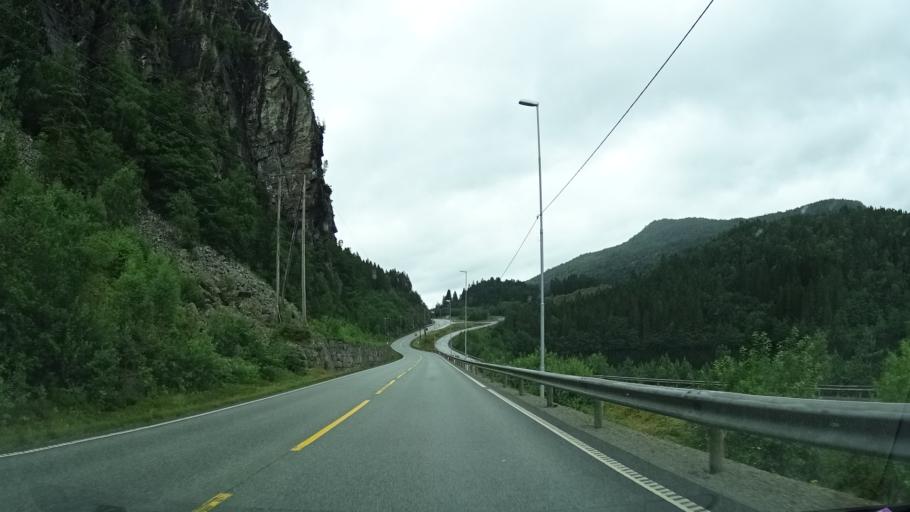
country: NO
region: Vest-Agder
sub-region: Flekkefjord
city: Flekkefjord
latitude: 58.3376
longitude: 6.6570
